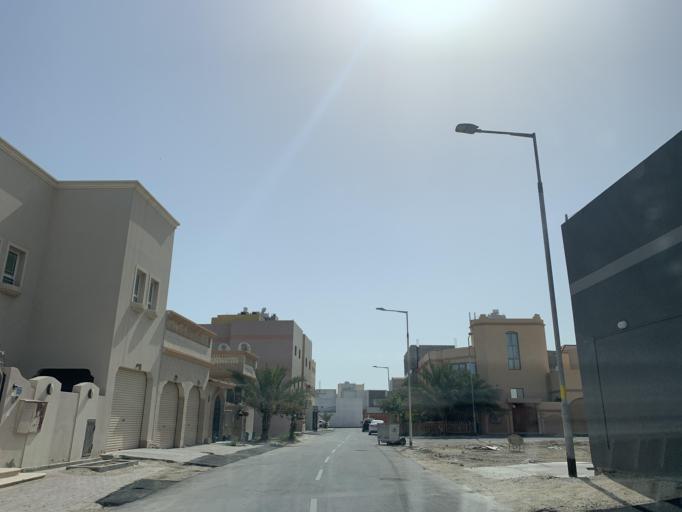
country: BH
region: Northern
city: Sitrah
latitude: 26.1461
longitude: 50.6042
